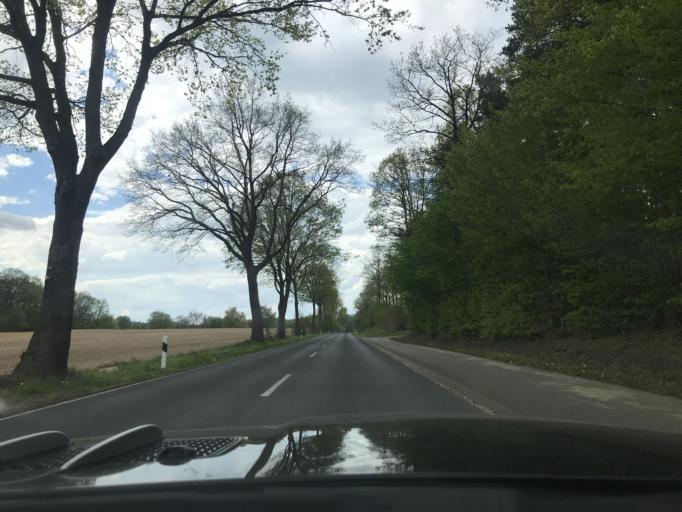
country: DE
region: Schleswig-Holstein
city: Gross Gronau
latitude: 53.7853
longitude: 10.7610
